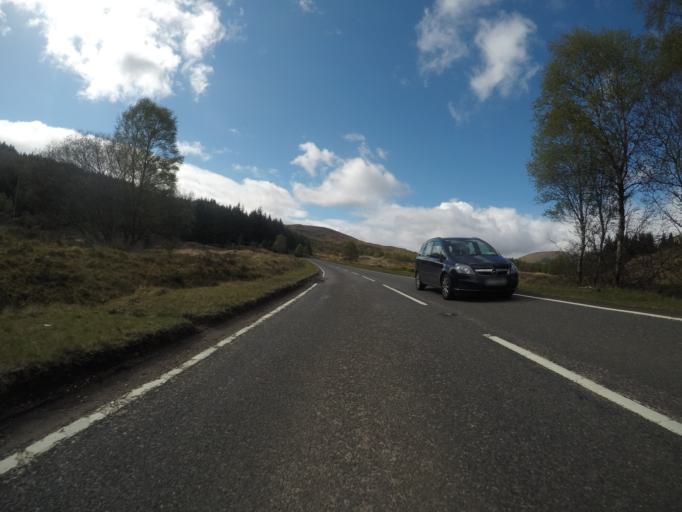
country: GB
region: Scotland
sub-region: Highland
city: Spean Bridge
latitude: 57.1300
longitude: -4.9620
